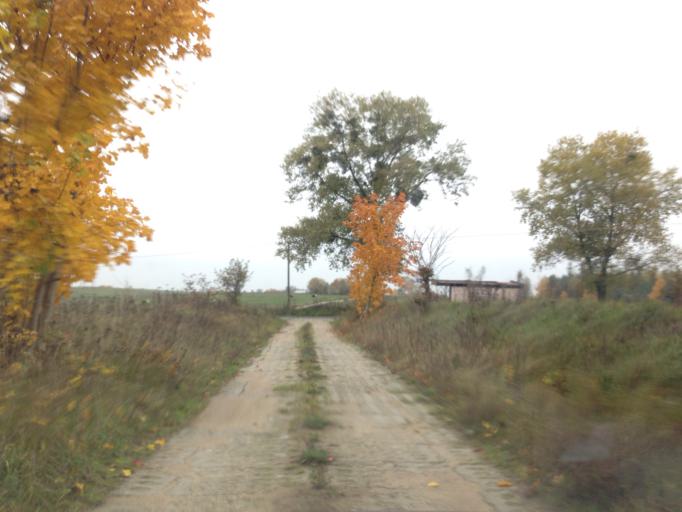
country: PL
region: Kujawsko-Pomorskie
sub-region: Powiat brodnicki
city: Gorzno
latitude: 53.2169
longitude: 19.6170
